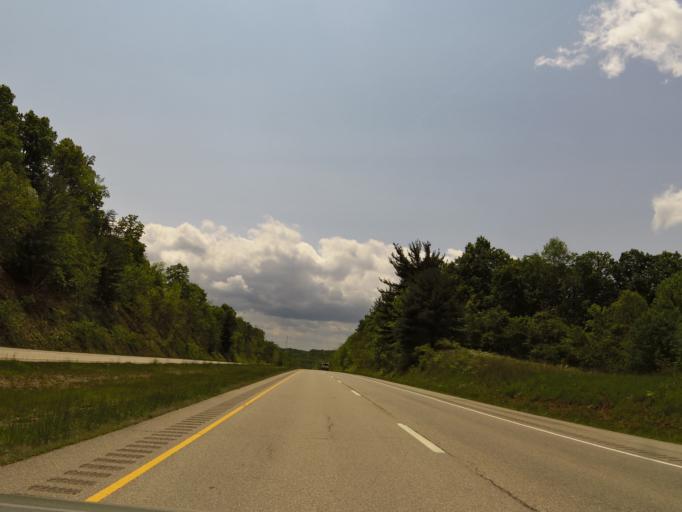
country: US
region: Ohio
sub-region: Meigs County
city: Pomeroy
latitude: 39.0878
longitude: -82.0159
